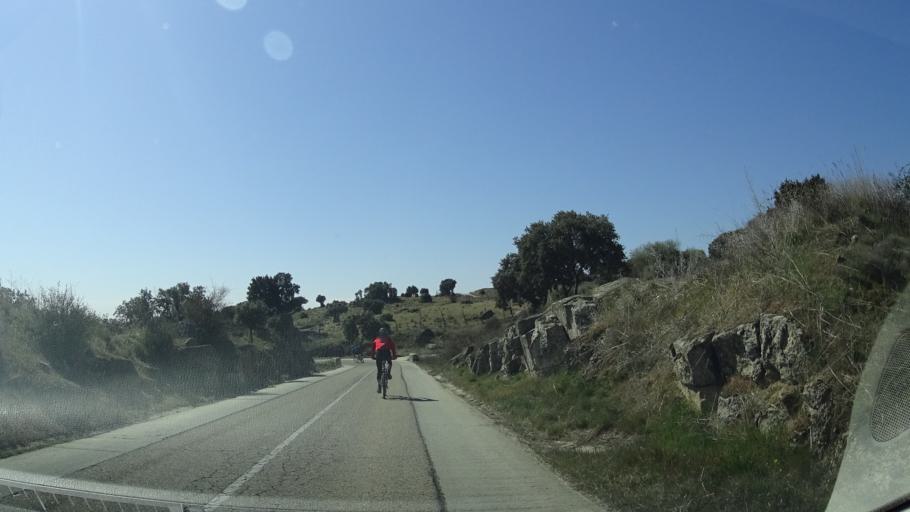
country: ES
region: Madrid
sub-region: Provincia de Madrid
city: Colmenar Viejo
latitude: 40.6434
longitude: -3.8140
